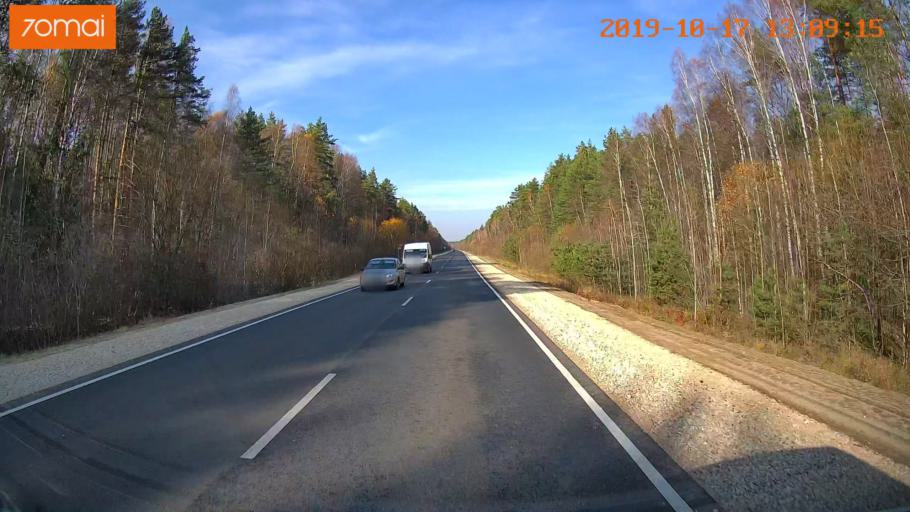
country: RU
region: Rjazan
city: Syntul
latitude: 55.0011
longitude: 41.2641
